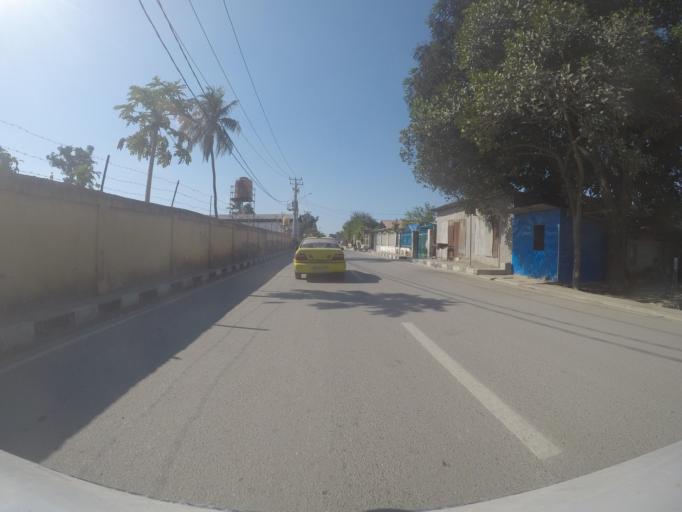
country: TL
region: Dili
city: Dili
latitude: -8.5650
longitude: 125.5558
